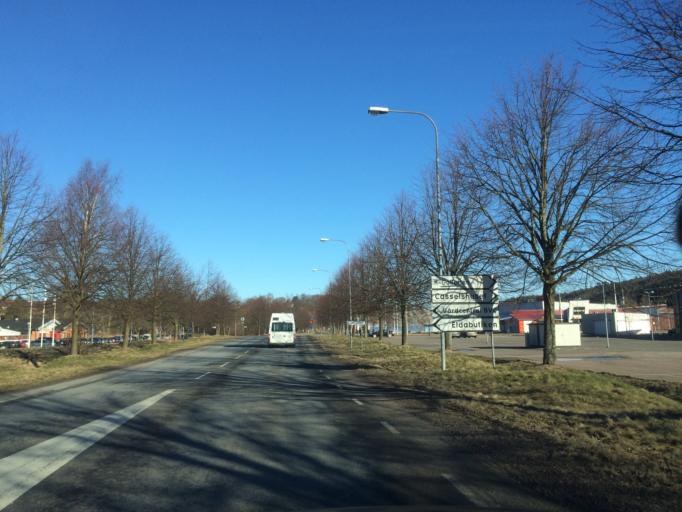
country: SE
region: Vaestra Goetaland
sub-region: Molndal
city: Kallered
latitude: 57.6067
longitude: 12.0444
